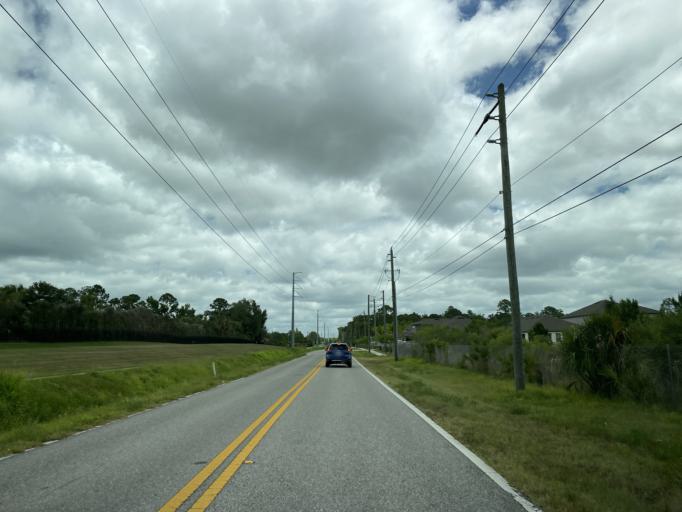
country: US
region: Florida
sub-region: Seminole County
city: Lake Mary
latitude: 28.8228
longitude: -81.3393
